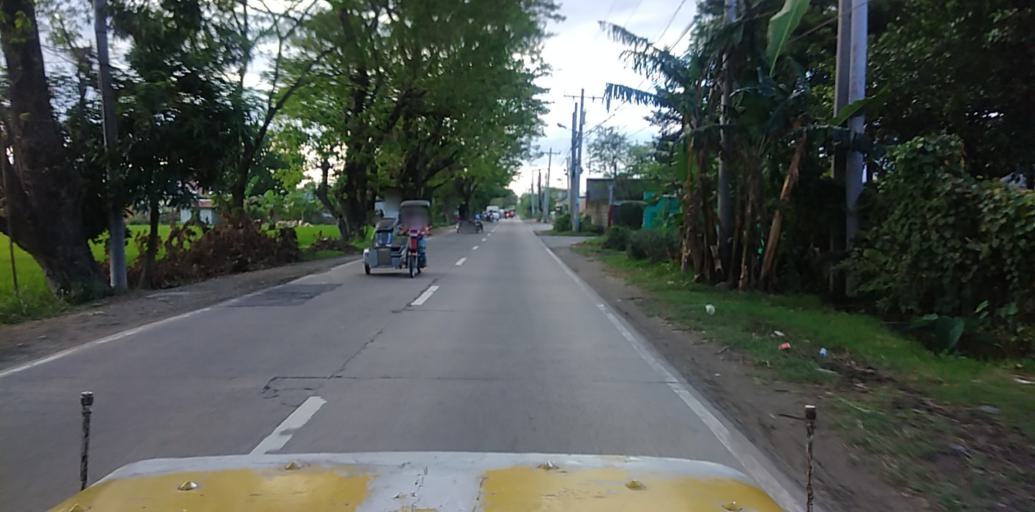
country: PH
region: Central Luzon
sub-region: Province of Pampanga
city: Arayat
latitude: 15.1524
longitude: 120.7374
